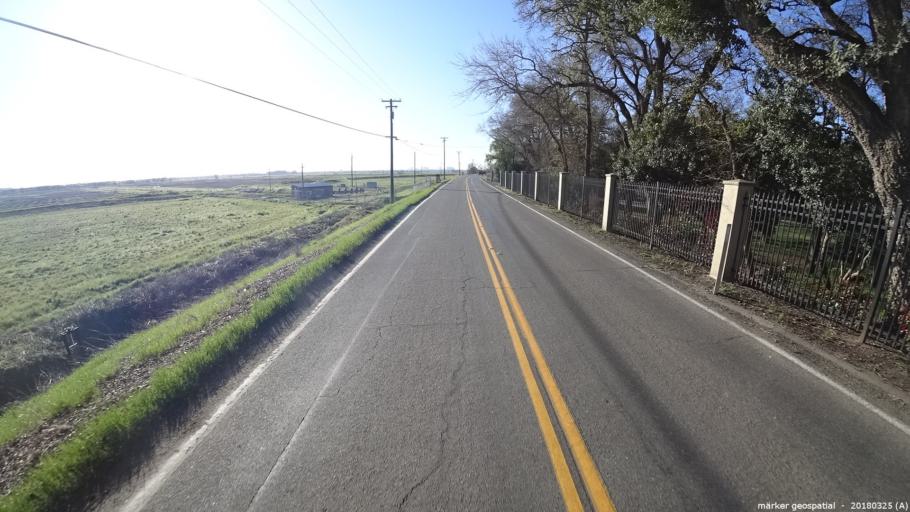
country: US
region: California
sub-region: Yolo County
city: West Sacramento
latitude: 38.6458
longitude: -121.5652
